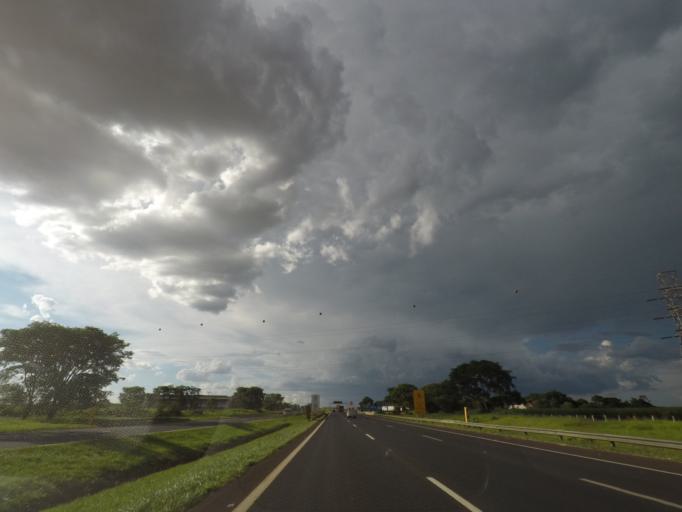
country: BR
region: Sao Paulo
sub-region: Ribeirao Preto
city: Ribeirao Preto
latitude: -21.1091
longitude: -47.7827
